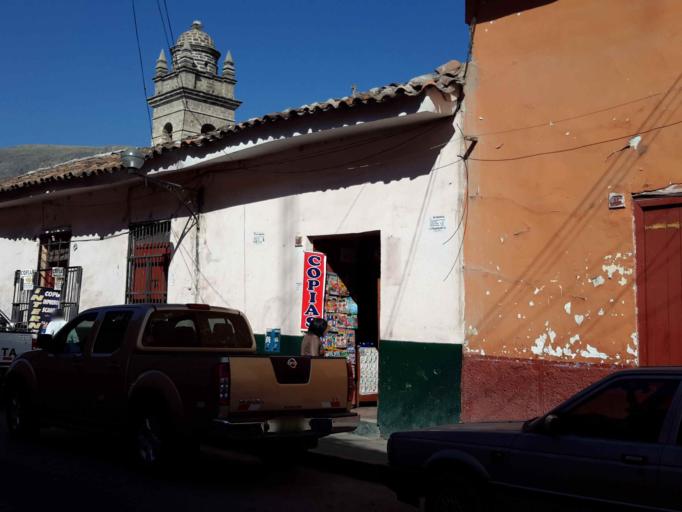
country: PE
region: Ayacucho
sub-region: Provincia de Huamanga
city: Ayacucho
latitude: -13.1642
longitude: -74.2272
